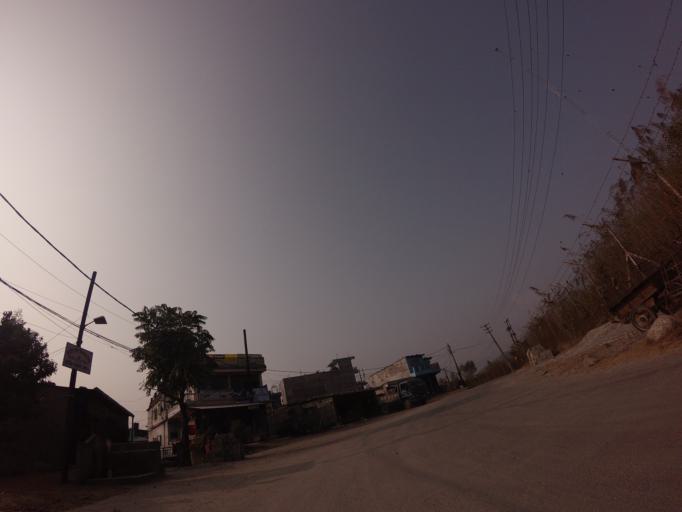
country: NP
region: Western Region
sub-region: Gandaki Zone
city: Pokhara
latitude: 28.2004
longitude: 83.9849
